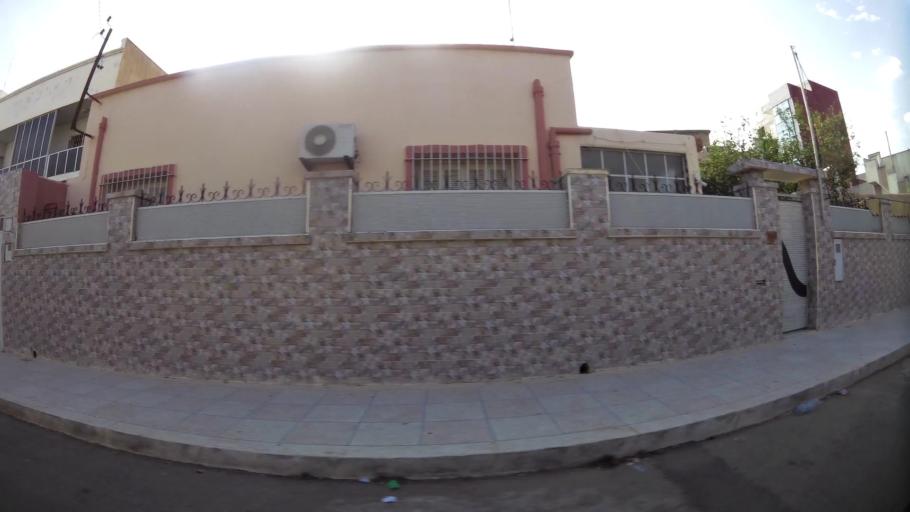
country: MA
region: Oriental
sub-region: Oujda-Angad
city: Oujda
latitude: 34.6743
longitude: -1.9196
